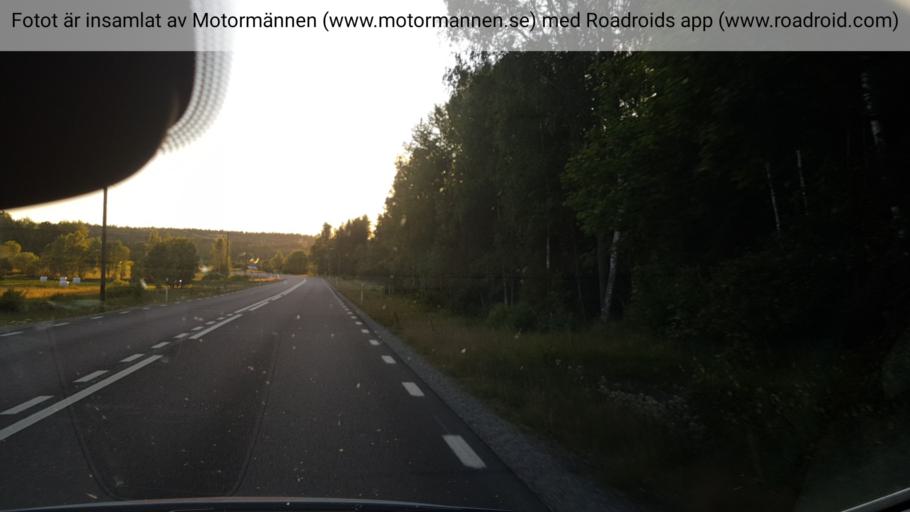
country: SE
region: Vaermland
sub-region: Sunne Kommun
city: Sunne
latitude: 59.6654
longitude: 12.9145
